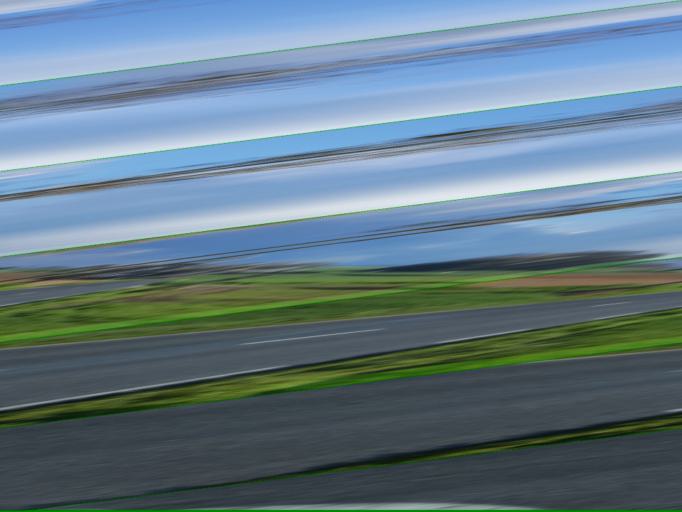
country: FR
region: Picardie
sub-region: Departement de l'Oise
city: Chaumont-en-Vexin
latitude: 49.2034
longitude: 1.8806
